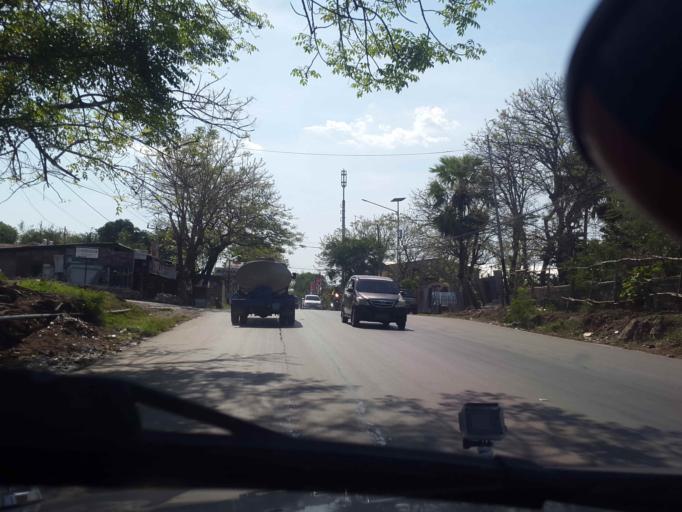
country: ID
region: East Nusa Tenggara
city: Kelapalima
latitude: -10.1442
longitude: 123.6244
